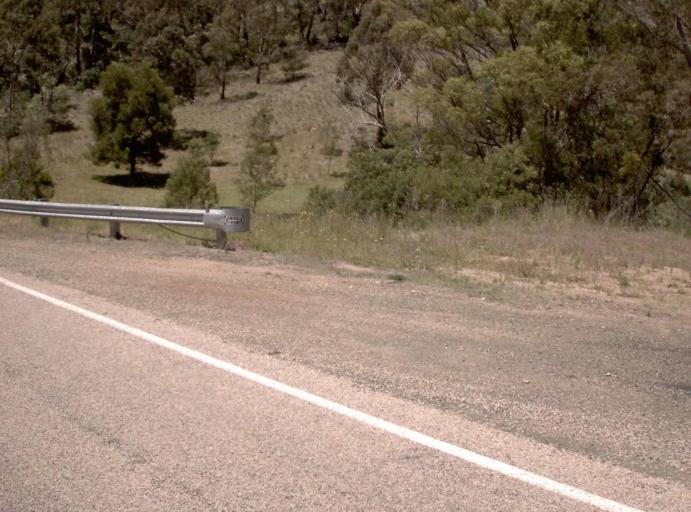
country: AU
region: Victoria
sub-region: Alpine
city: Mount Beauty
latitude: -37.1654
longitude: 147.6589
